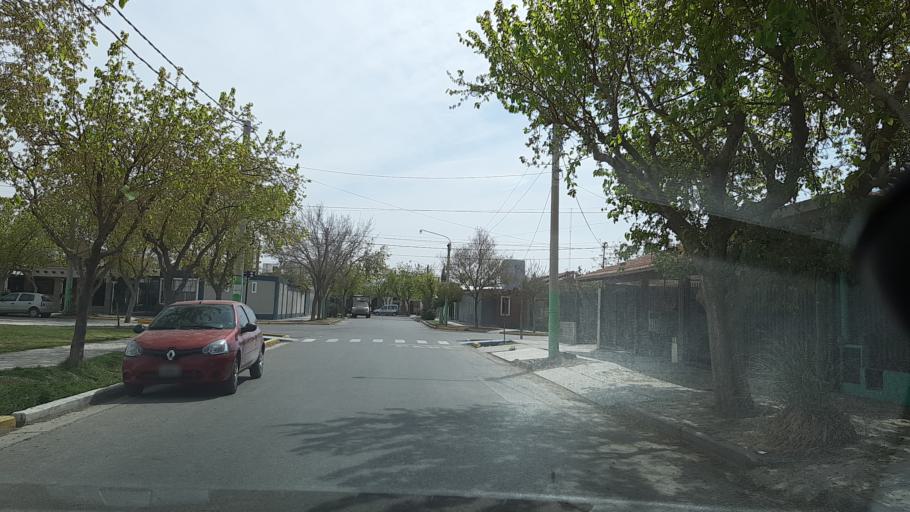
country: AR
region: San Juan
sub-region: Departamento de Rivadavia
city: Rivadavia
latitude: -31.5348
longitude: -68.5995
